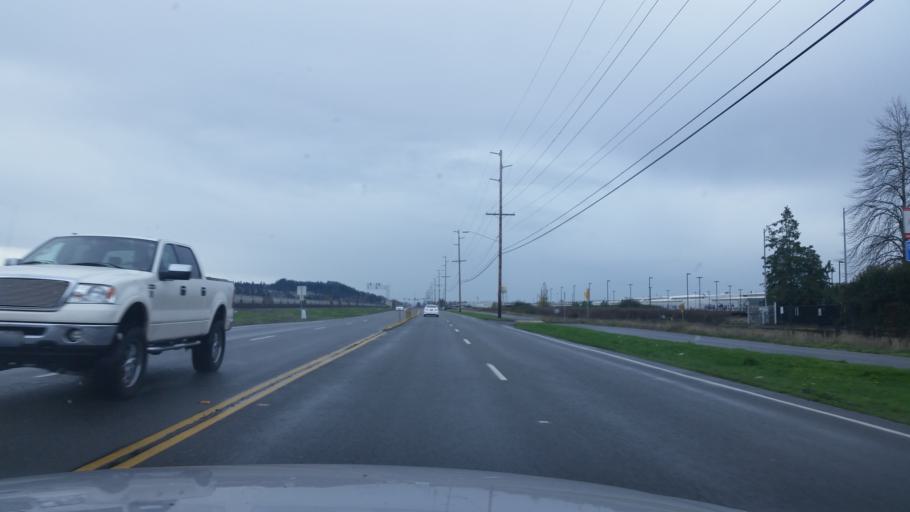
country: US
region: Washington
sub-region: King County
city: Auburn
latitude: 47.2945
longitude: -122.2321
